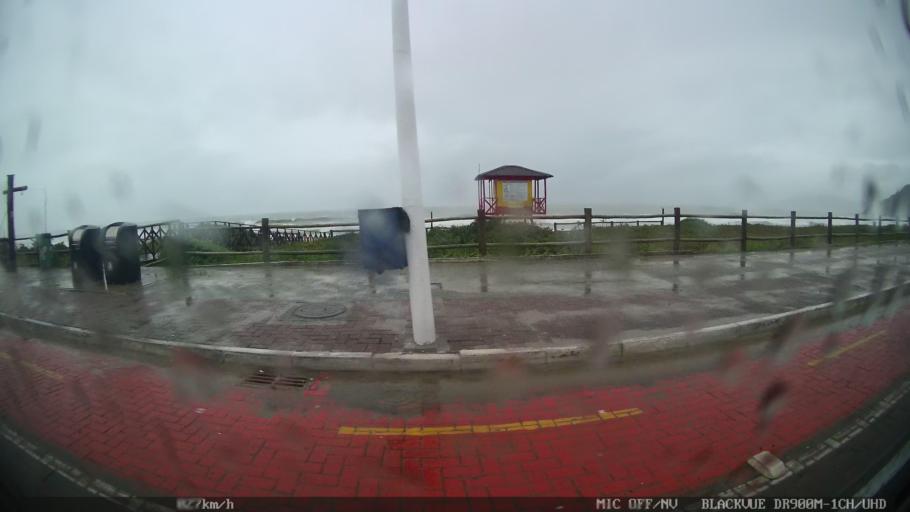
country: BR
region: Santa Catarina
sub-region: Balneario Camboriu
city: Balneario Camboriu
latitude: -26.9513
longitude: -48.6296
